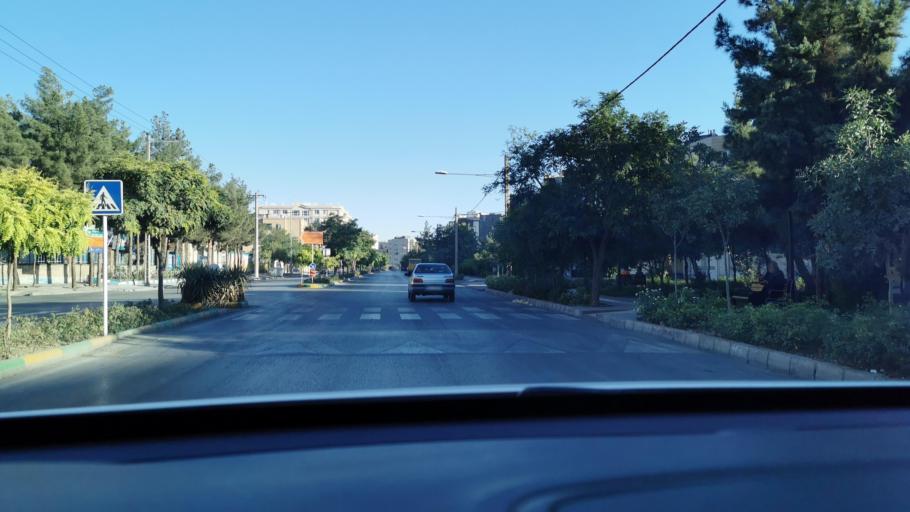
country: IR
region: Razavi Khorasan
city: Mashhad
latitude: 36.3579
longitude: 59.4860
